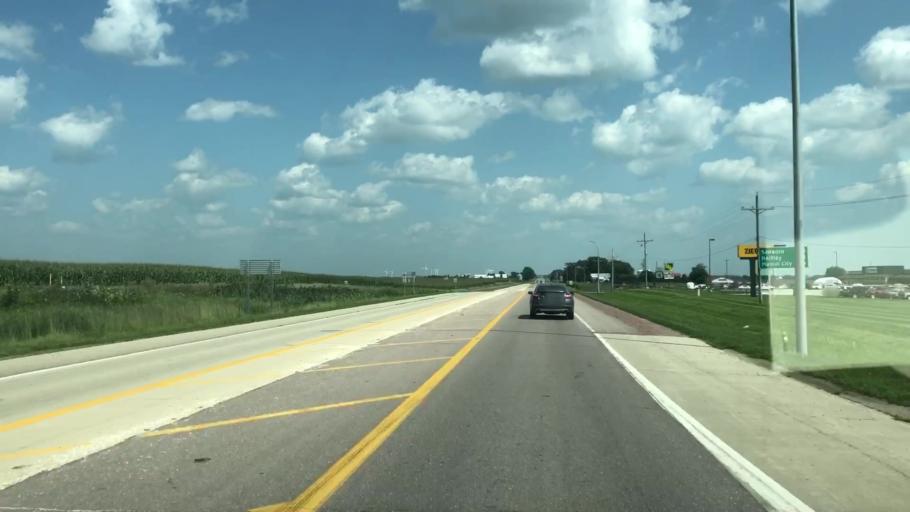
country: US
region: Iowa
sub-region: O'Brien County
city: Sheldon
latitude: 43.1860
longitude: -95.8113
